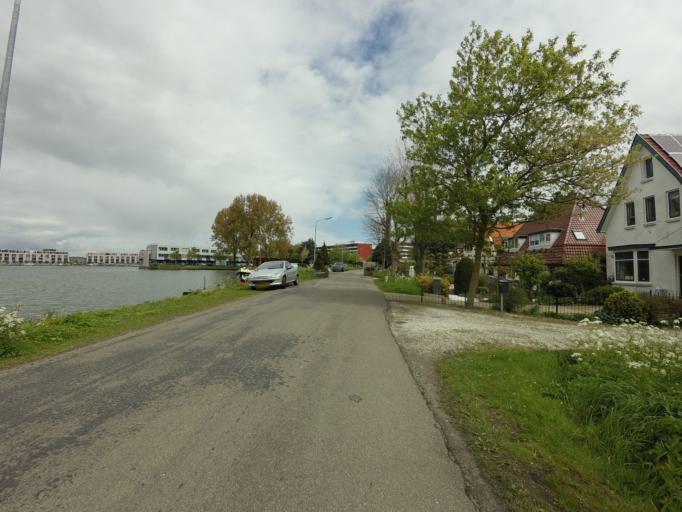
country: NL
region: North Holland
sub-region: Gemeente Amsterdam
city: Driemond
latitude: 52.3069
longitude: 5.0257
